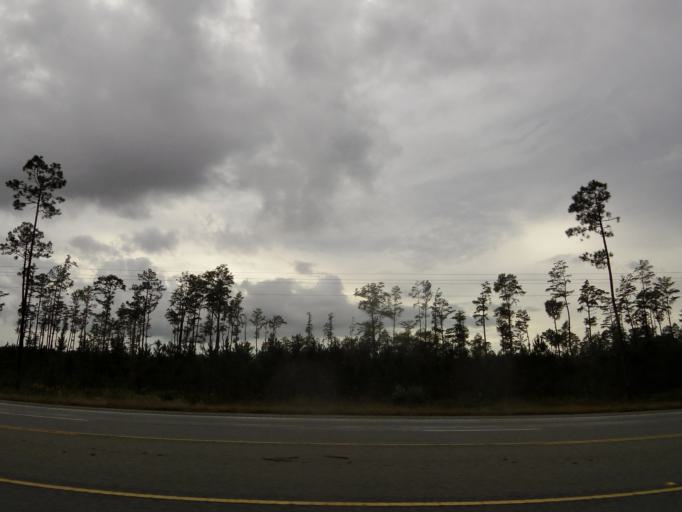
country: US
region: Georgia
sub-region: Wayne County
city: Jesup
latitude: 31.5503
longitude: -81.8124
